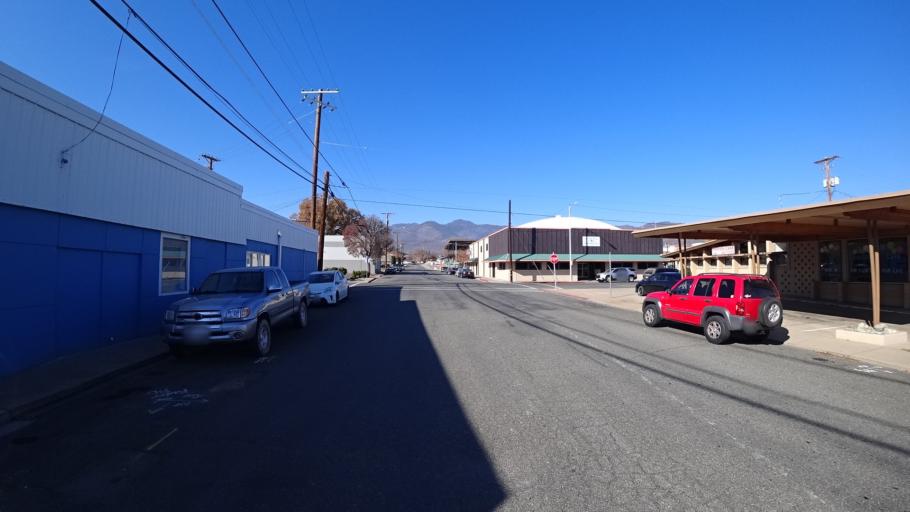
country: US
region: California
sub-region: Siskiyou County
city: Yreka
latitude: 41.7284
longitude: -122.6370
